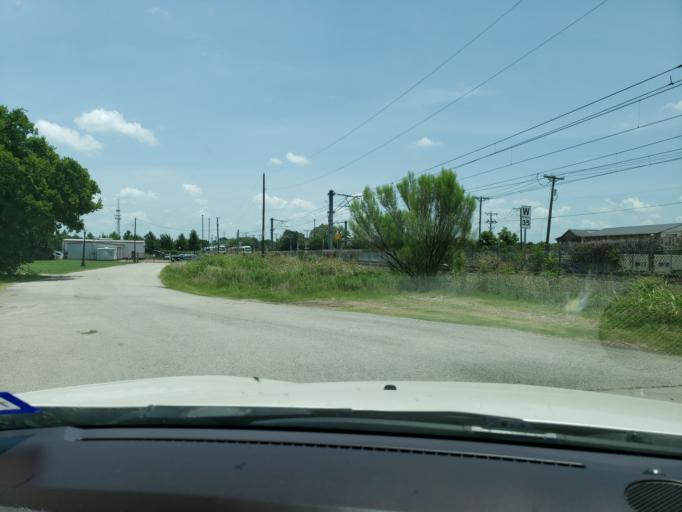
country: US
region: Texas
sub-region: Dallas County
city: Rowlett
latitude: 32.9040
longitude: -96.5664
